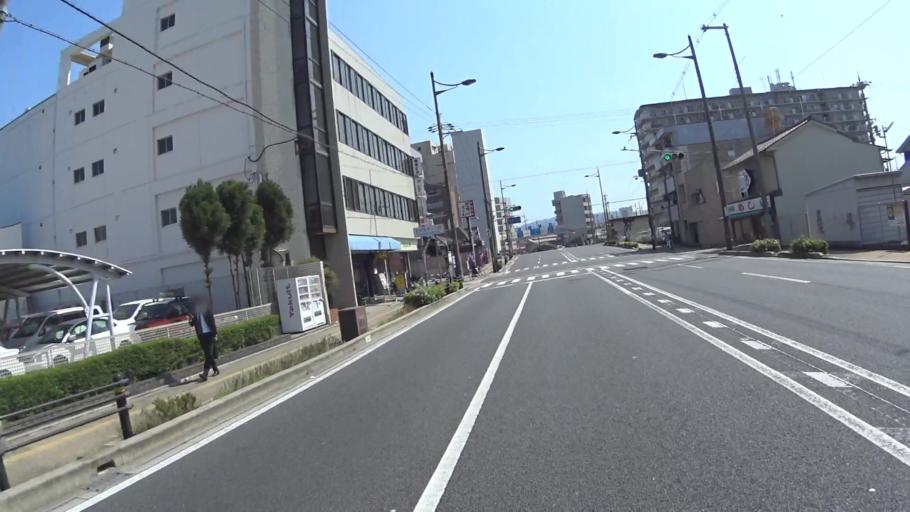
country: JP
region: Kyoto
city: Muko
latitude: 34.9775
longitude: 135.7307
